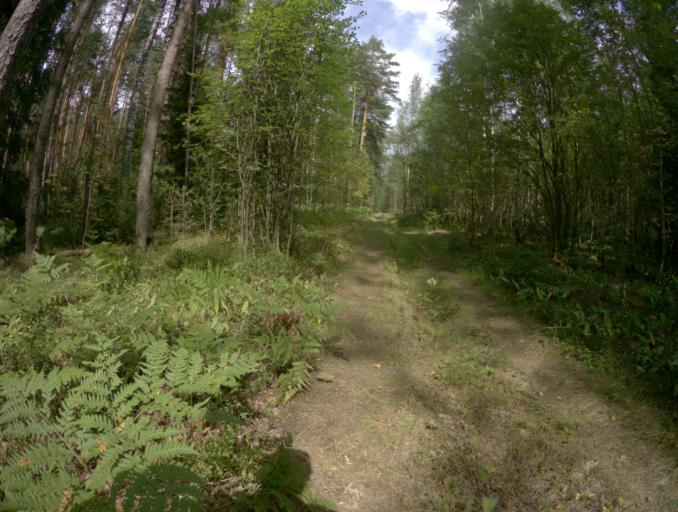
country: RU
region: Vladimir
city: Raduzhnyy
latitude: 55.9652
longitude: 40.2202
